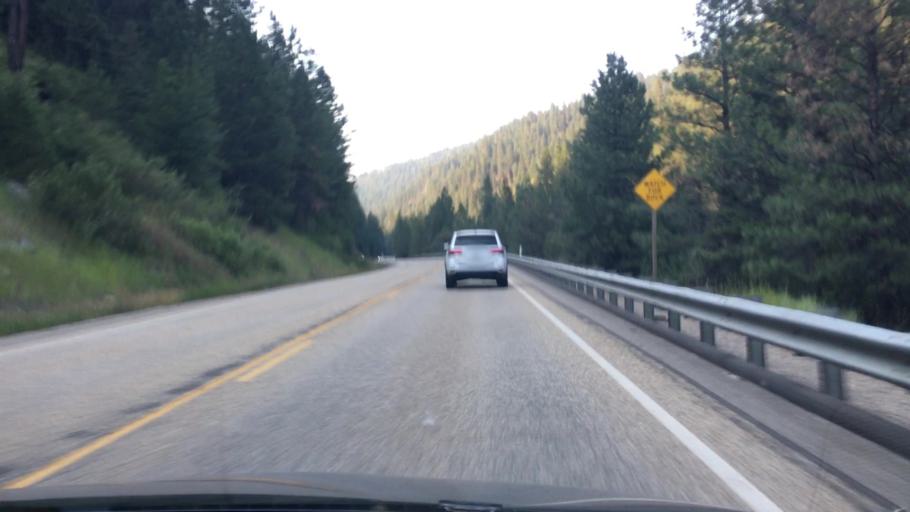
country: US
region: Idaho
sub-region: Valley County
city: Cascade
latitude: 44.1986
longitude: -116.1130
